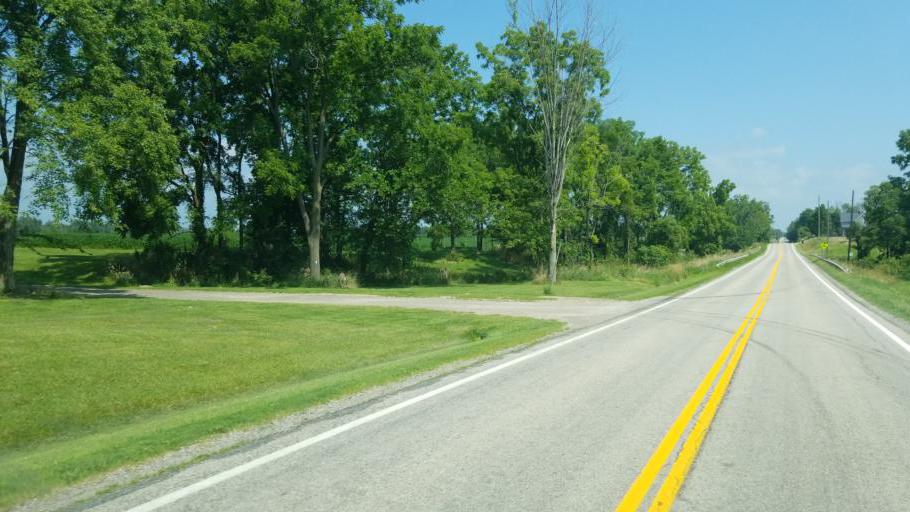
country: US
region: Ohio
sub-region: Crawford County
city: Galion
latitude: 40.8294
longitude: -82.8556
